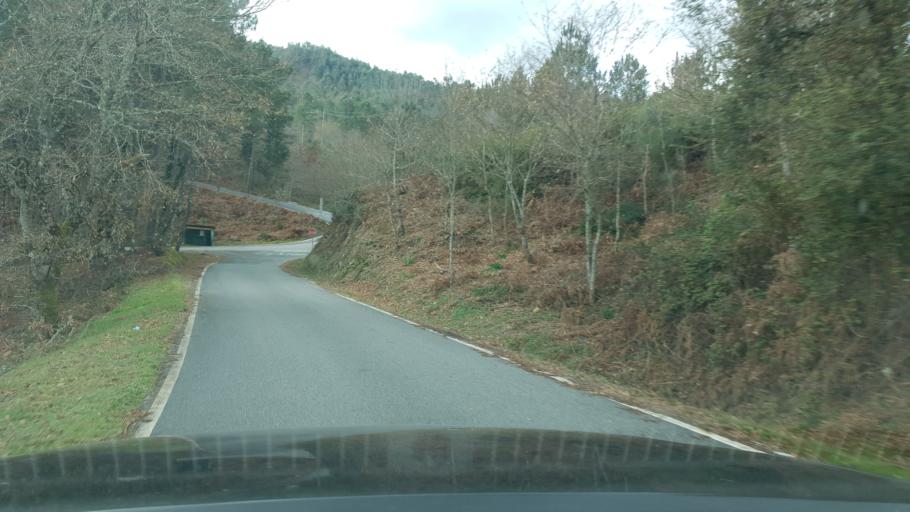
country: PT
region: Viseu
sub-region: Castro Daire
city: Castro Daire
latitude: 40.8847
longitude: -8.0197
